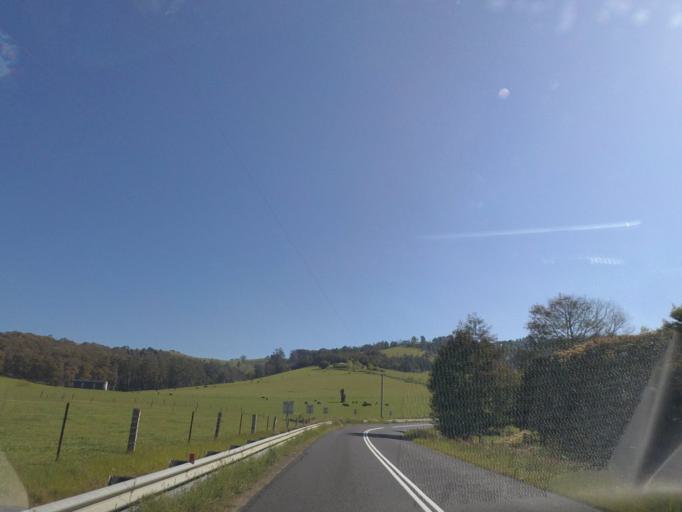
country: AU
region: Victoria
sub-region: Baw Baw
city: Warragul
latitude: -37.9003
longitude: 145.9705
